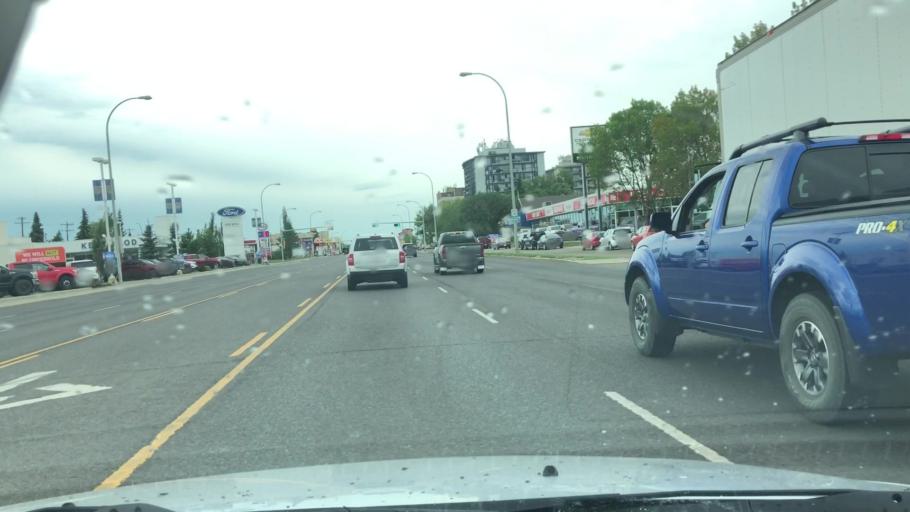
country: CA
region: Alberta
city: Edmonton
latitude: 53.5932
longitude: -113.4920
